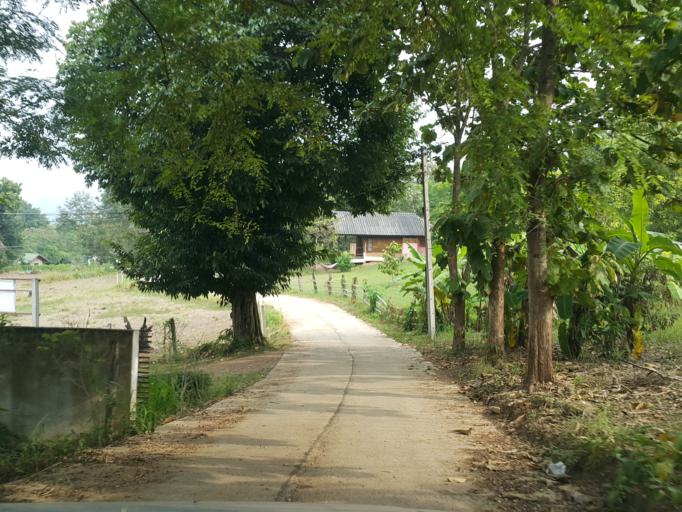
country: TH
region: Mae Hong Son
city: Wiang Nuea
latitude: 19.3718
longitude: 98.4469
